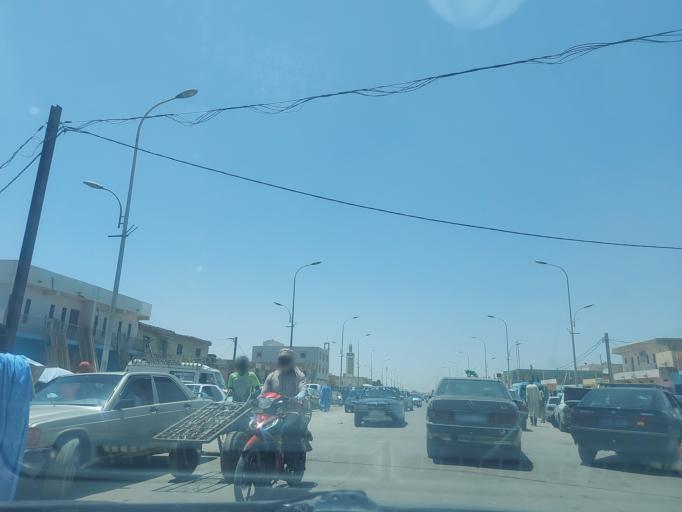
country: MR
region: Nouakchott
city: Nouakchott
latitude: 18.0816
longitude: -15.9815
